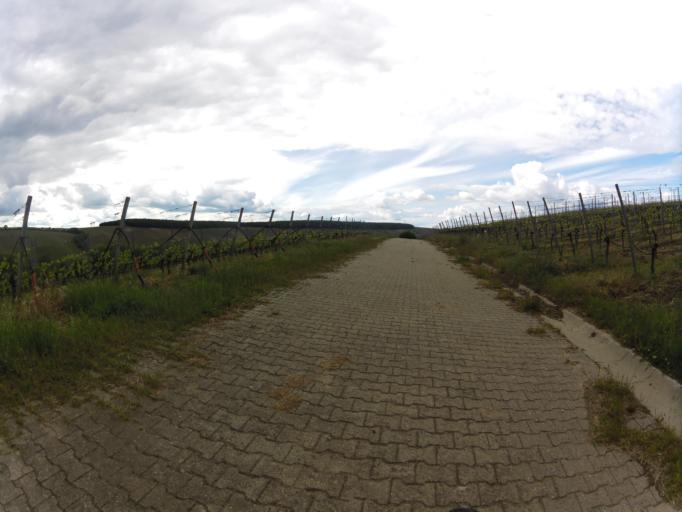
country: DE
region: Bavaria
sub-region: Regierungsbezirk Unterfranken
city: Sommerach
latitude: 49.8400
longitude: 10.1852
